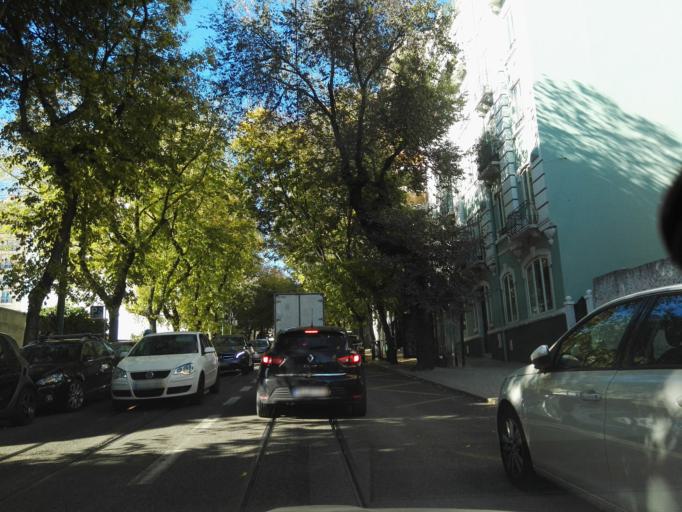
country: PT
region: Lisbon
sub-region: Lisbon
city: Lisbon
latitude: 38.7144
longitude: -9.1620
